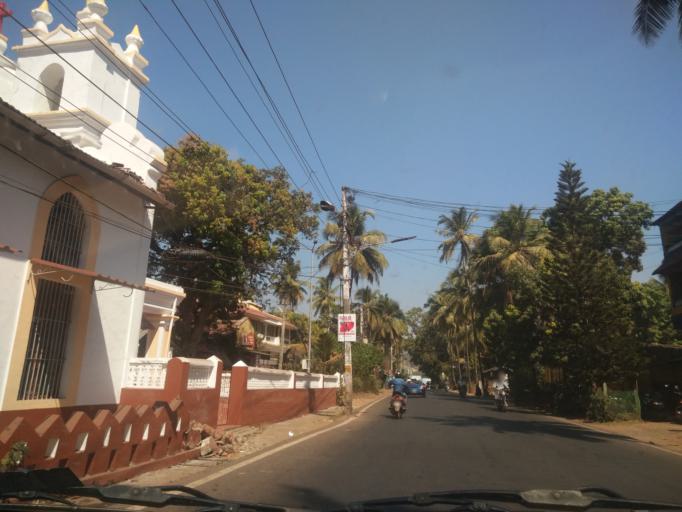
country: IN
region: Goa
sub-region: North Goa
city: Guirim
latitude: 15.5785
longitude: 73.8062
